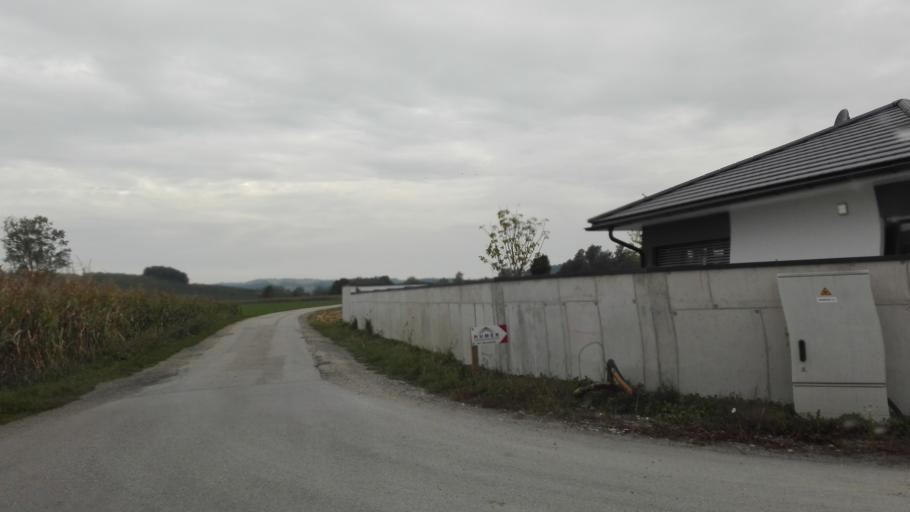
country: AT
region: Upper Austria
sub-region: Wels-Land
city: Buchkirchen
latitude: 48.2827
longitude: 14.0241
